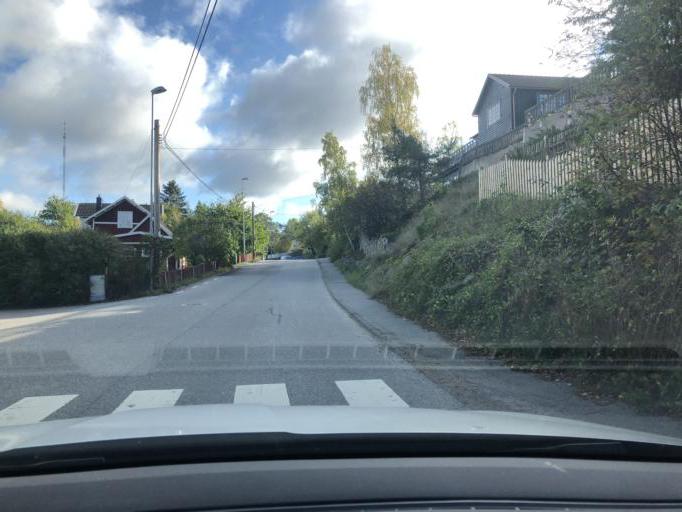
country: SE
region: Stockholm
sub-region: Nacka Kommun
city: Nacka
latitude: 59.2983
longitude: 18.1551
